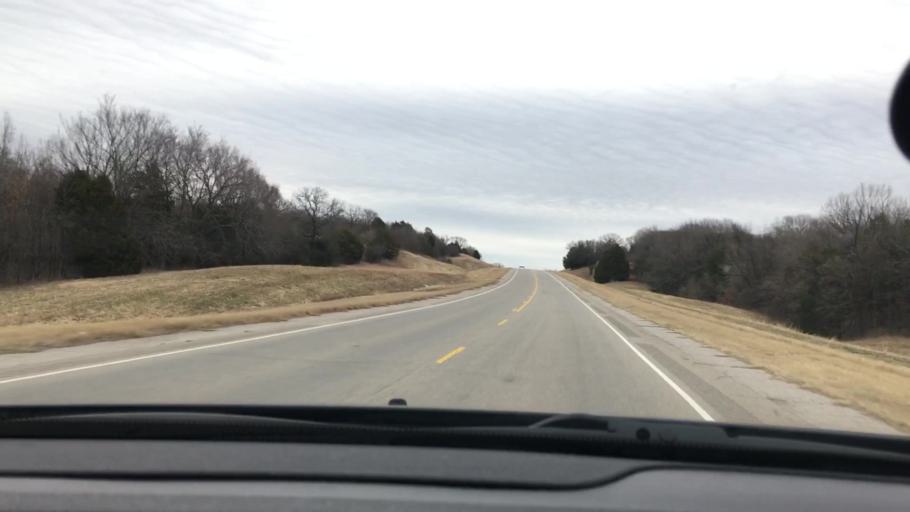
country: US
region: Oklahoma
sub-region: Johnston County
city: Tishomingo
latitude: 34.2355
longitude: -96.7804
